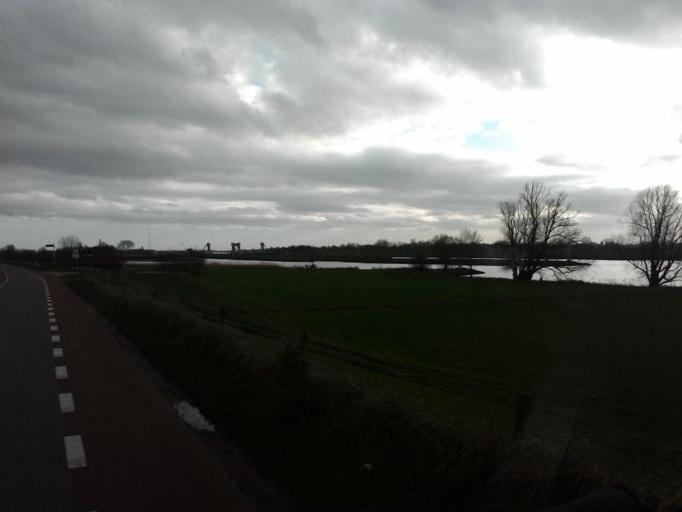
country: NL
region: Utrecht
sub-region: Gemeente Vianen
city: Vianen
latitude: 52.0008
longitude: 5.1259
